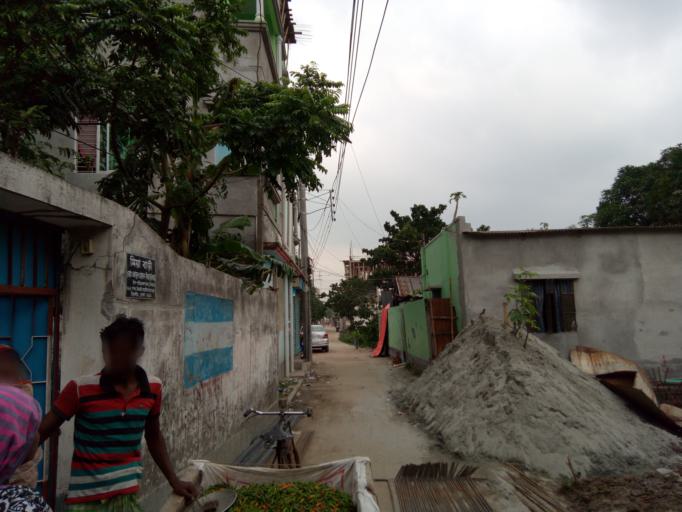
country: BD
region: Dhaka
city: Paltan
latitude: 23.7555
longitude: 90.4516
